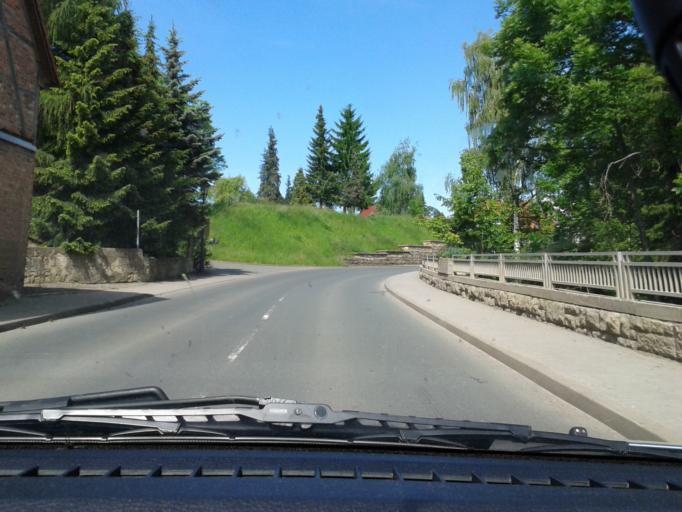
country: DE
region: Thuringia
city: Eberstedt
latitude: 51.0287
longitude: 11.5609
